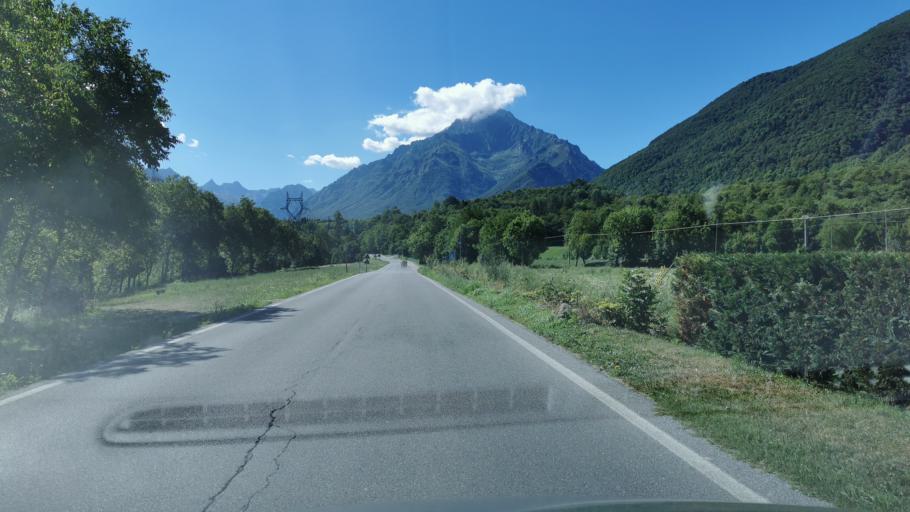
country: IT
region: Piedmont
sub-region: Provincia di Cuneo
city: Valdieri
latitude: 44.2587
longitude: 7.3829
